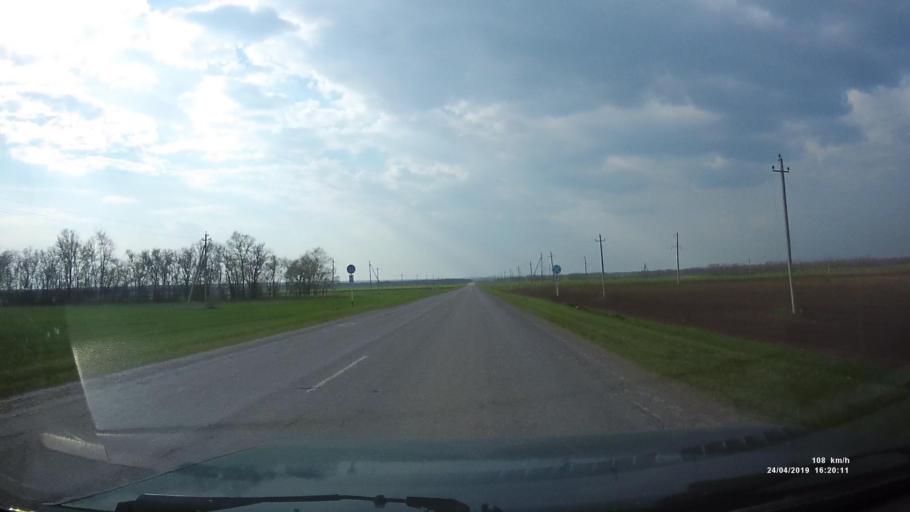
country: RU
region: Rostov
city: Orlovskiy
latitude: 46.7891
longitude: 42.0840
